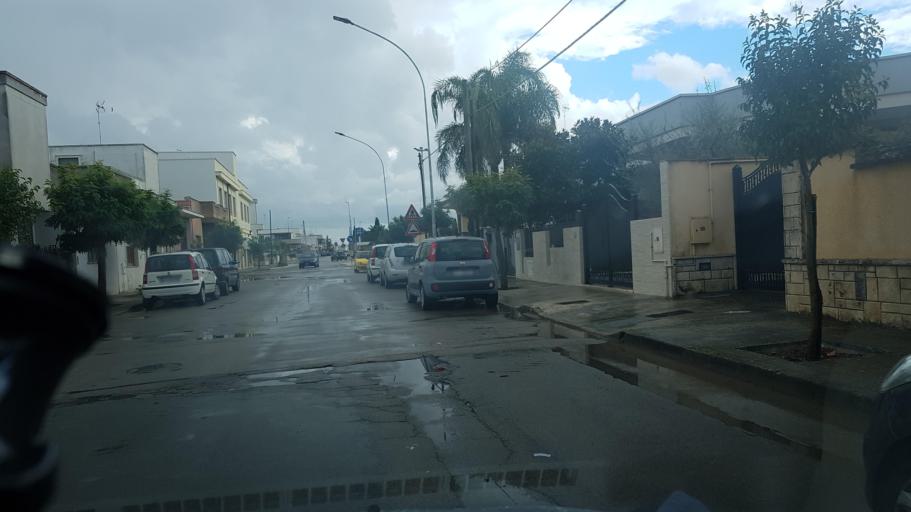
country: IT
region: Apulia
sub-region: Provincia di Lecce
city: Carmiano
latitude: 40.3391
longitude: 18.0408
